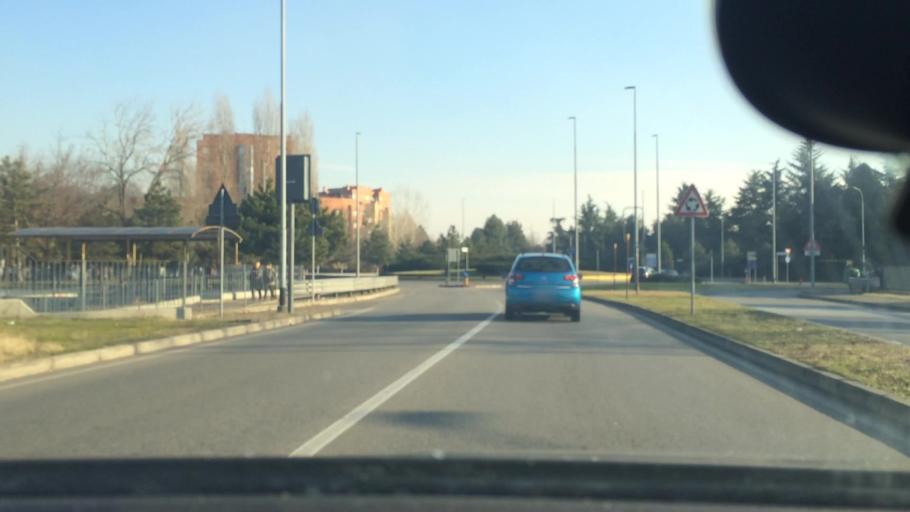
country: IT
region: Lombardy
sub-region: Citta metropolitana di Milano
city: Passirana
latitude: 45.5367
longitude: 9.0221
